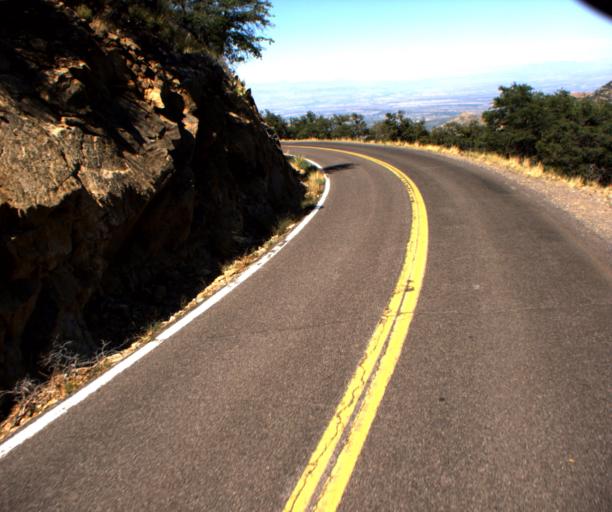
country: US
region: Arizona
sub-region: Graham County
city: Swift Trail Junction
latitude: 32.6494
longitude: -109.8090
